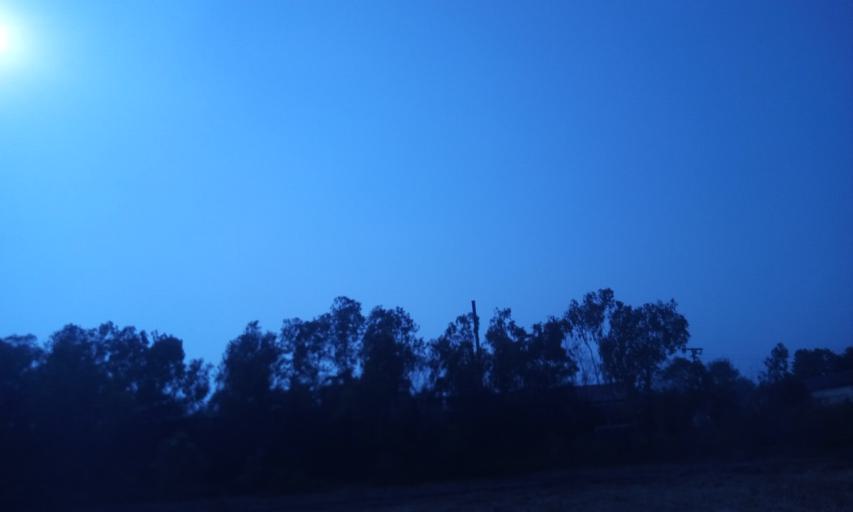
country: TH
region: Nonthaburi
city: Sai Noi
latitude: 13.9777
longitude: 100.3211
